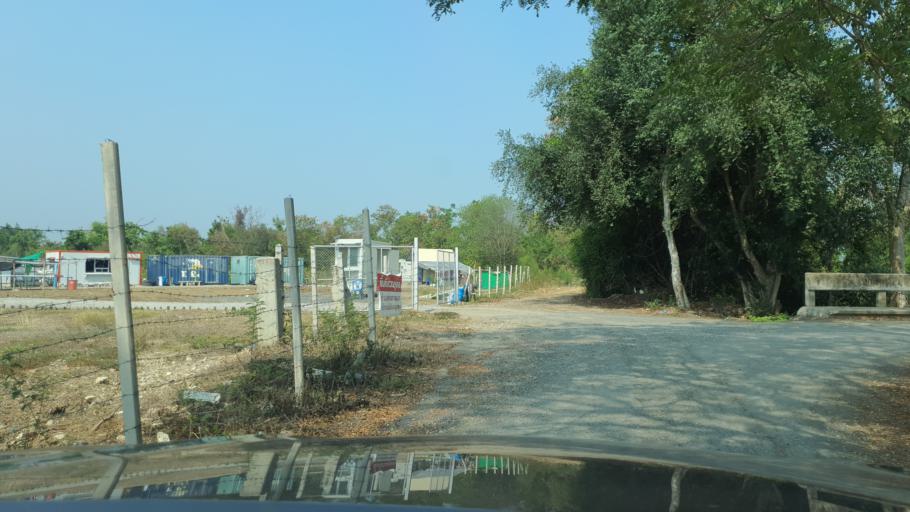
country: TH
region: Chiang Mai
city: Saraphi
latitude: 18.7314
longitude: 99.0709
